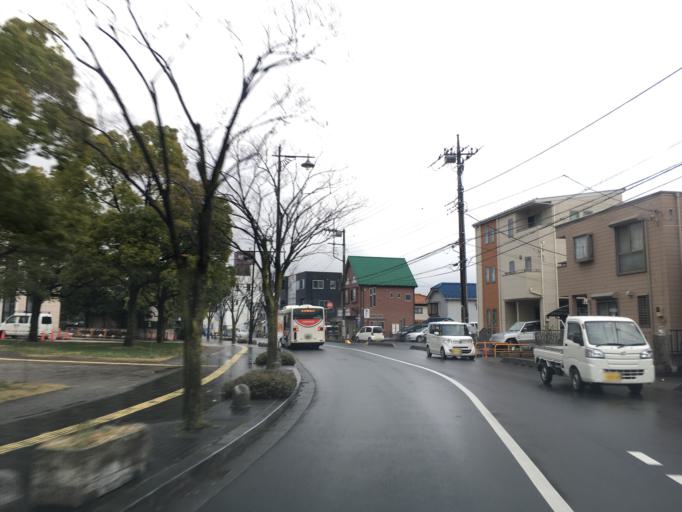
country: JP
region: Saitama
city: Koshigaya
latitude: 35.8897
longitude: 139.7909
